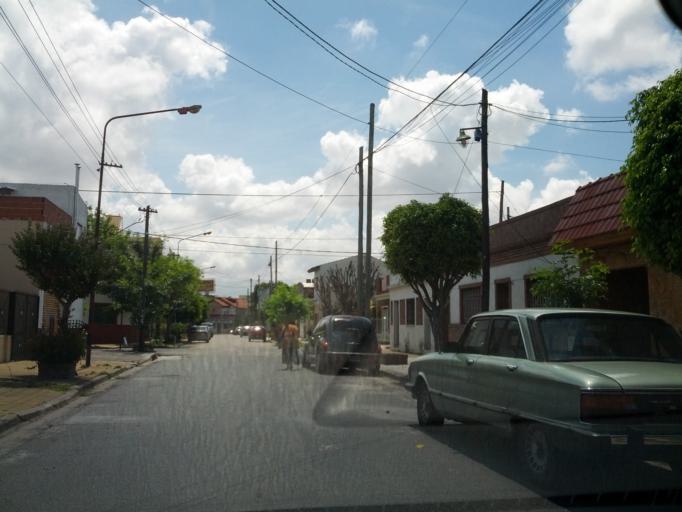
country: AR
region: Buenos Aires
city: San Justo
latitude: -34.6445
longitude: -58.5454
